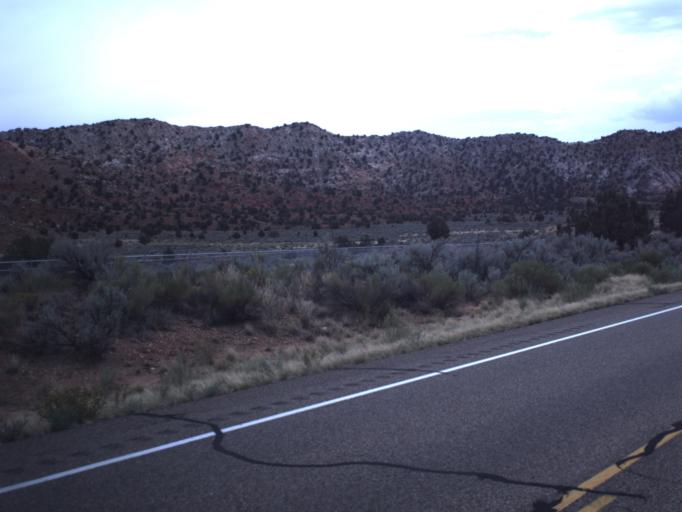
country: US
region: Utah
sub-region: Kane County
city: Kanab
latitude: 37.1601
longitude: -111.9696
